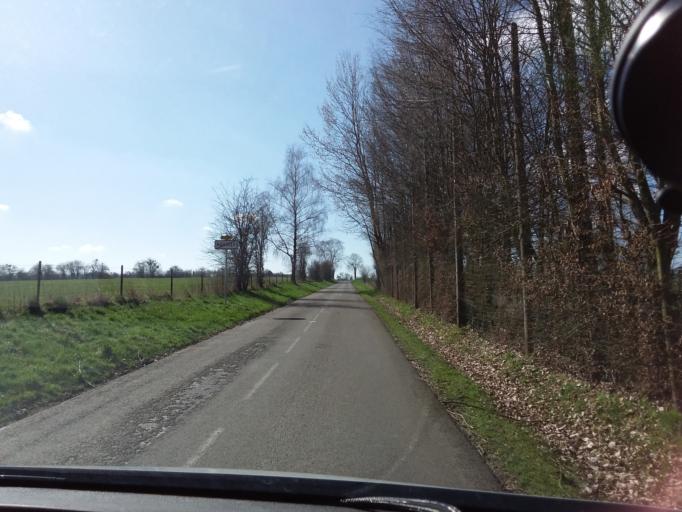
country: FR
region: Picardie
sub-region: Departement de l'Aisne
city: Hirson
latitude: 49.8742
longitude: 4.0916
